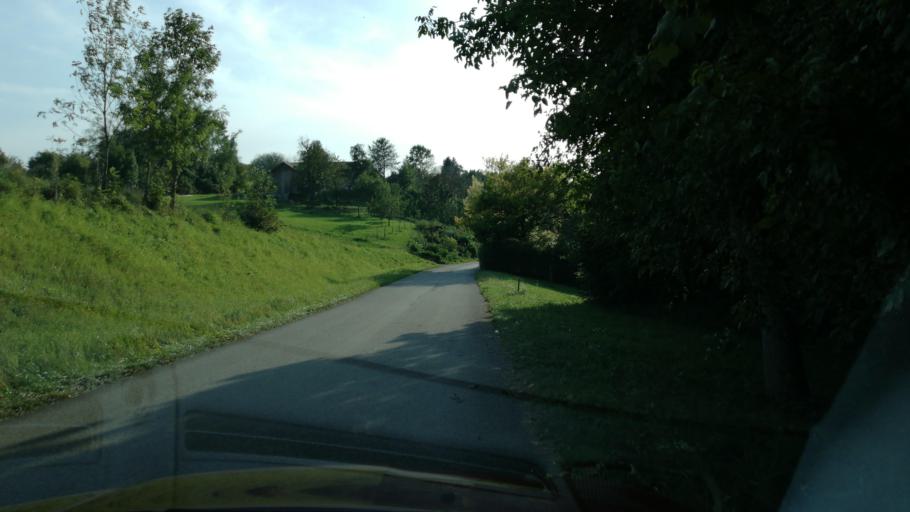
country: AT
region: Upper Austria
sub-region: Politischer Bezirk Steyr-Land
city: Sierning
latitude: 48.1067
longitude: 14.3200
